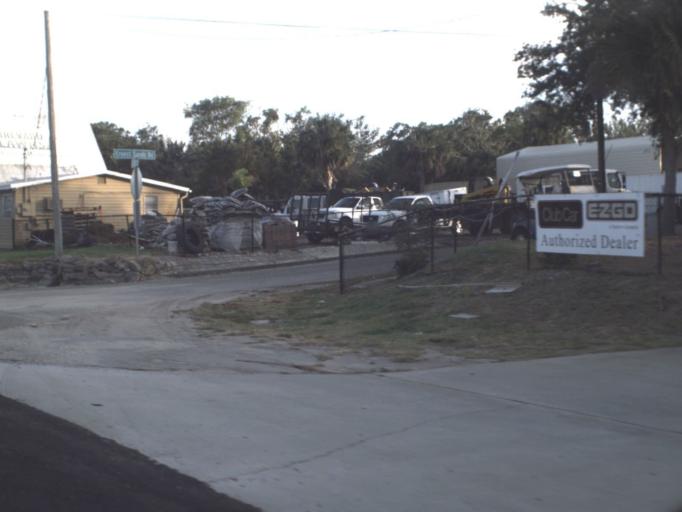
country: US
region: Florida
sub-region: Brevard County
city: South Patrick Shores
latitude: 28.2347
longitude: -80.6753
